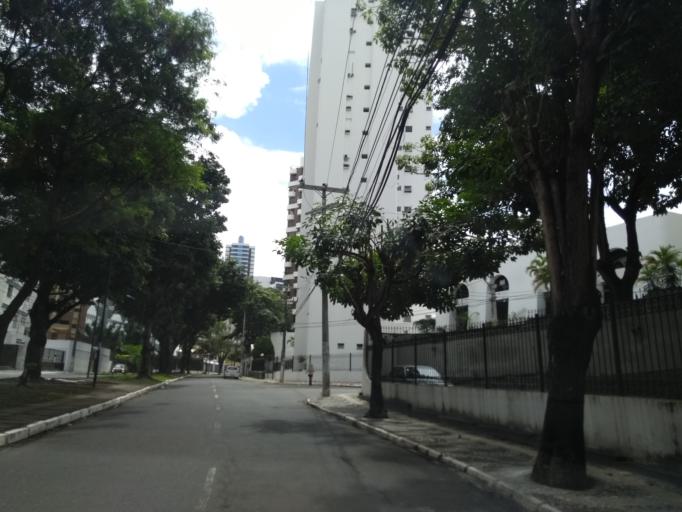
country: BR
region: Bahia
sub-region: Salvador
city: Salvador
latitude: -13.0050
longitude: -38.5198
